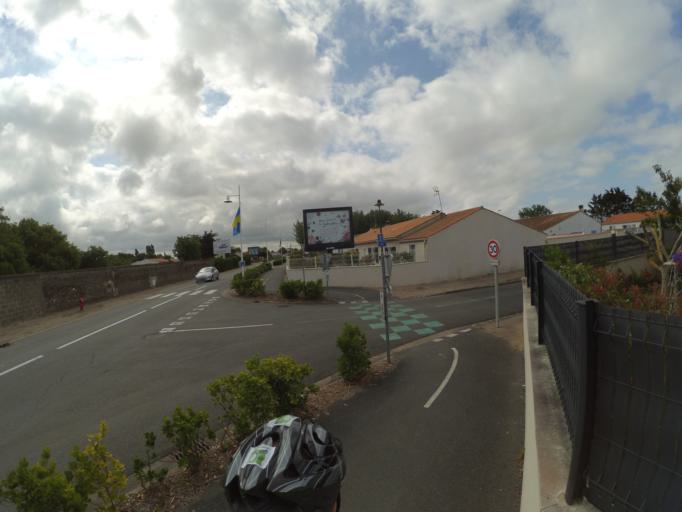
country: FR
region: Poitou-Charentes
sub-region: Departement de la Charente-Maritime
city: Chatelaillon-Plage
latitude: 46.0880
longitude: -1.0966
